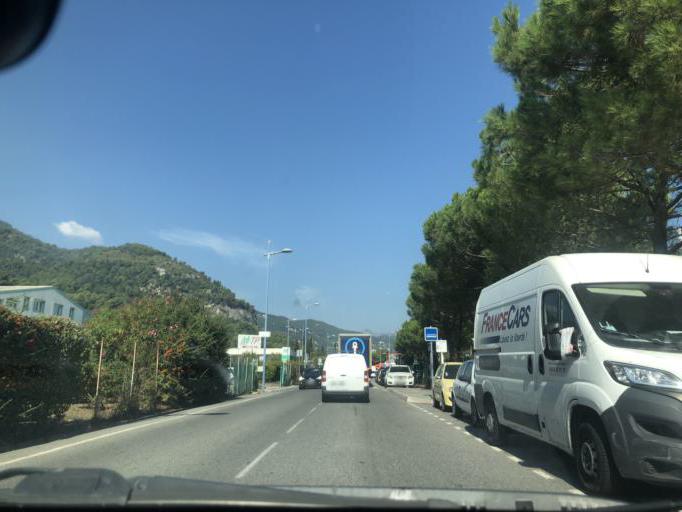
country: FR
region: Provence-Alpes-Cote d'Azur
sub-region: Departement des Alpes-Maritimes
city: Carros
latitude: 43.7938
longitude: 7.2019
